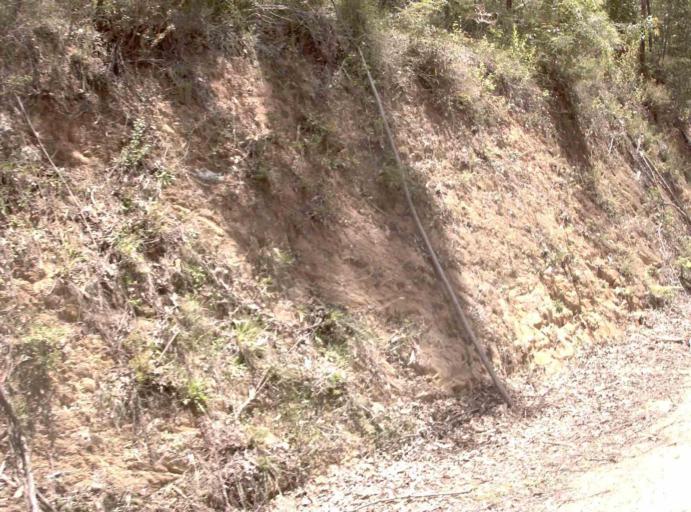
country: AU
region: New South Wales
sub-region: Bombala
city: Bombala
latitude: -37.5576
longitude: 148.9437
